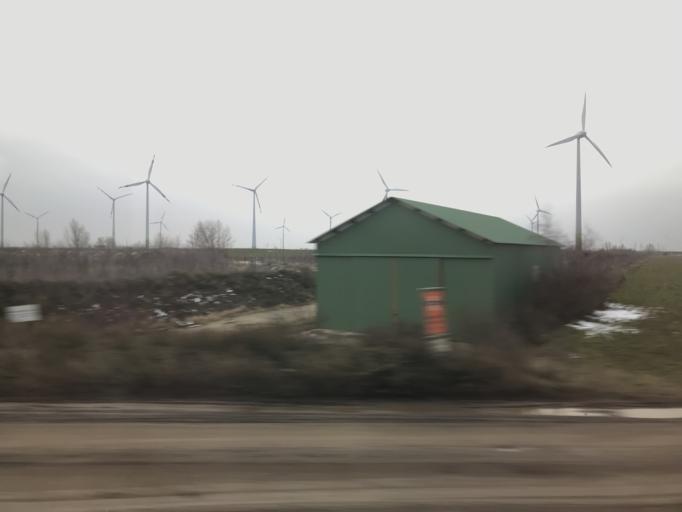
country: AT
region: Burgenland
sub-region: Politischer Bezirk Neusiedl am See
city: Parndorf
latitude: 47.9885
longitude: 16.9088
